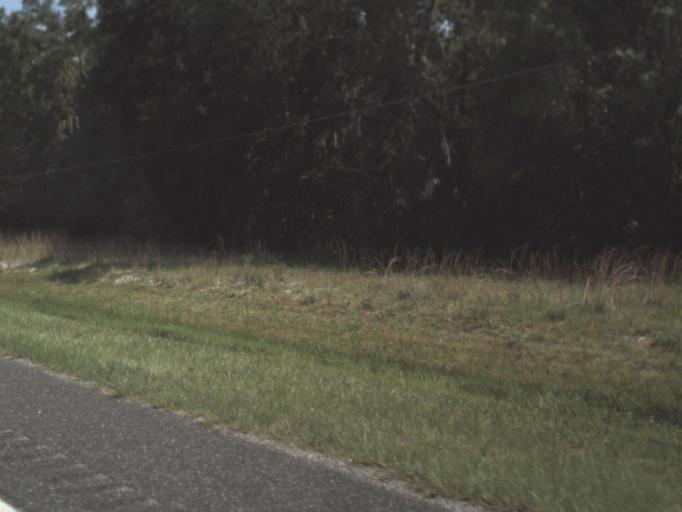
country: US
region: Florida
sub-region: Alachua County
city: Gainesville
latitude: 29.5197
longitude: -82.2990
